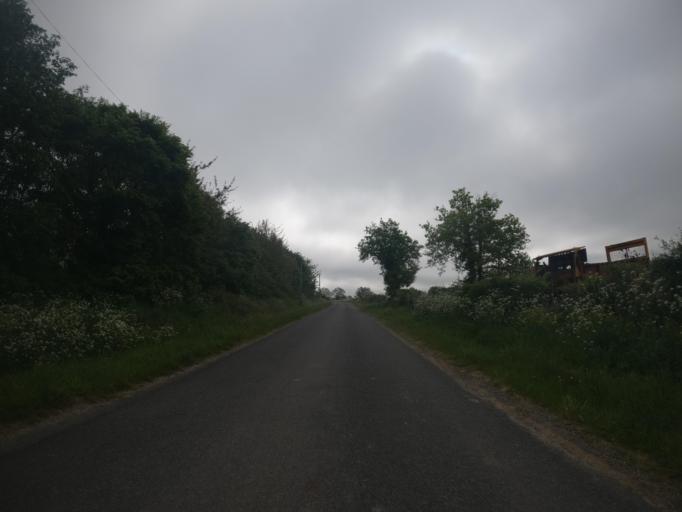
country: FR
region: Poitou-Charentes
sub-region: Departement des Deux-Sevres
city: Chiche
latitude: 46.8240
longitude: -0.3772
